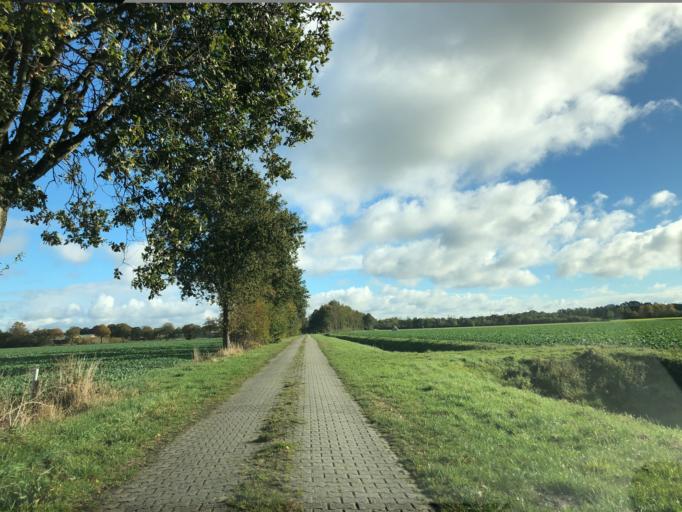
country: DE
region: Lower Saxony
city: Lehe
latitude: 53.0358
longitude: 7.3629
